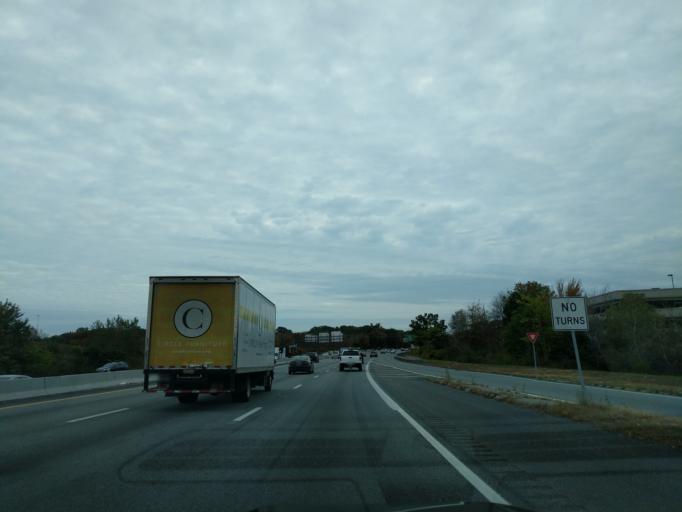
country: US
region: Massachusetts
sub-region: Middlesex County
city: Reading
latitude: 42.5183
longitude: -71.0884
